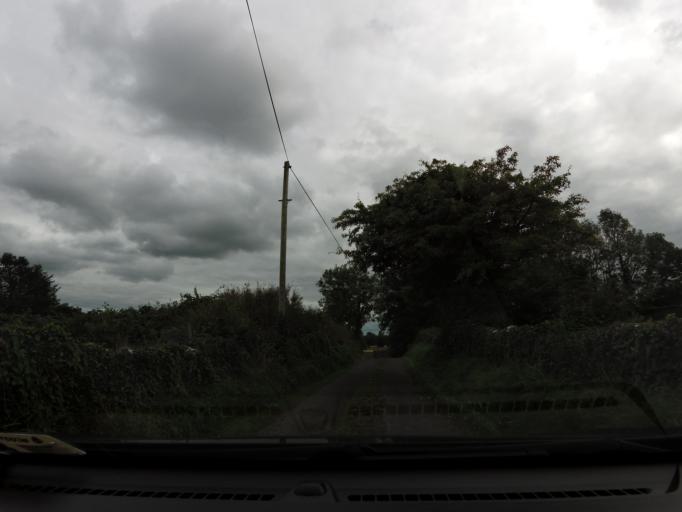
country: IE
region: Connaught
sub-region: County Galway
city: Loughrea
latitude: 53.1535
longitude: -8.4638
